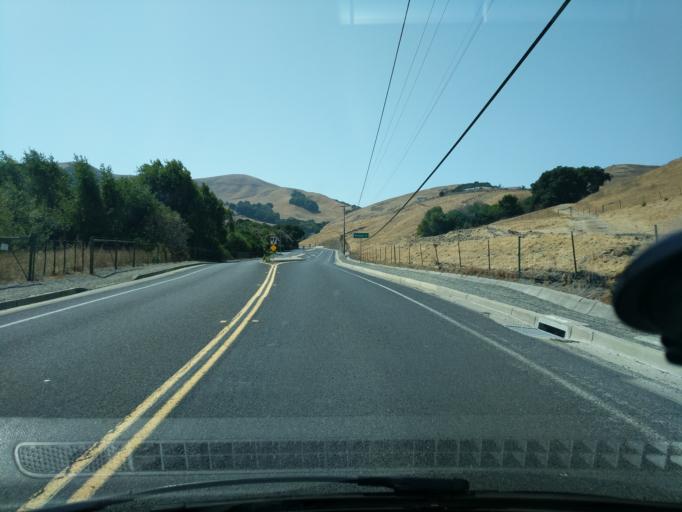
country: US
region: California
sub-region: Contra Costa County
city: San Ramon
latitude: 37.7579
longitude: -121.9987
